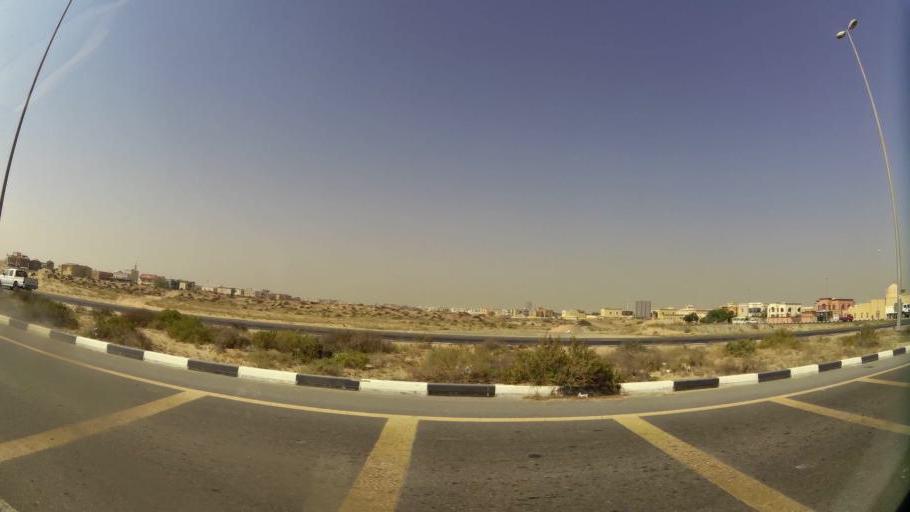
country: AE
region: Ajman
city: Ajman
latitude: 25.4223
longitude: 55.5317
